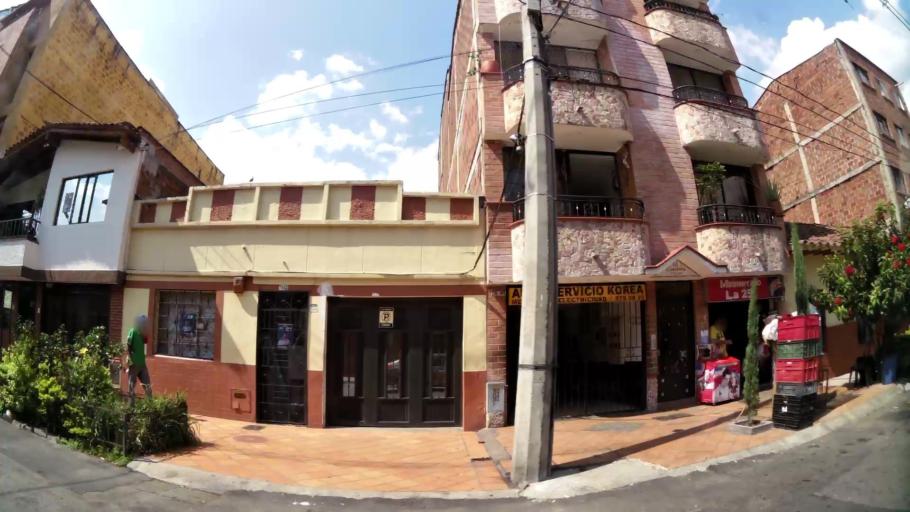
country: CO
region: Antioquia
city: Medellin
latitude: 6.2306
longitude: -75.5942
